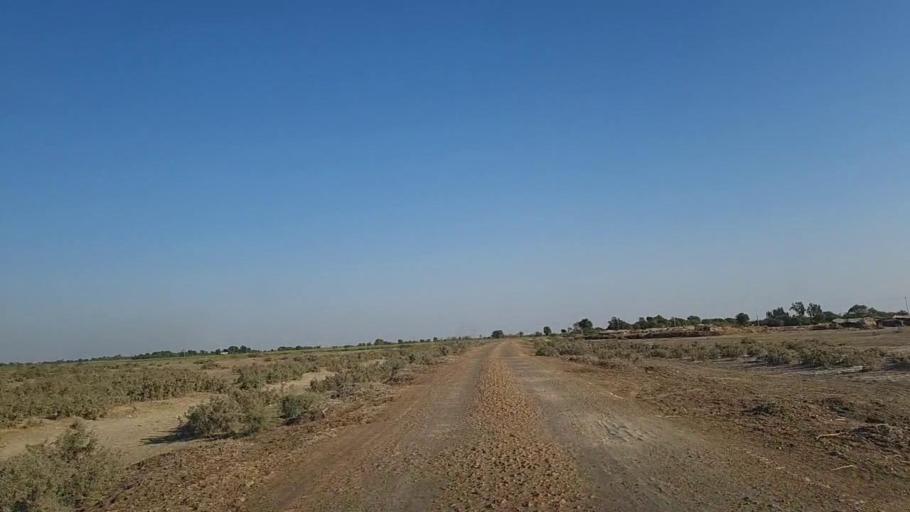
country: PK
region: Sindh
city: Naukot
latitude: 24.9724
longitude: 69.3788
